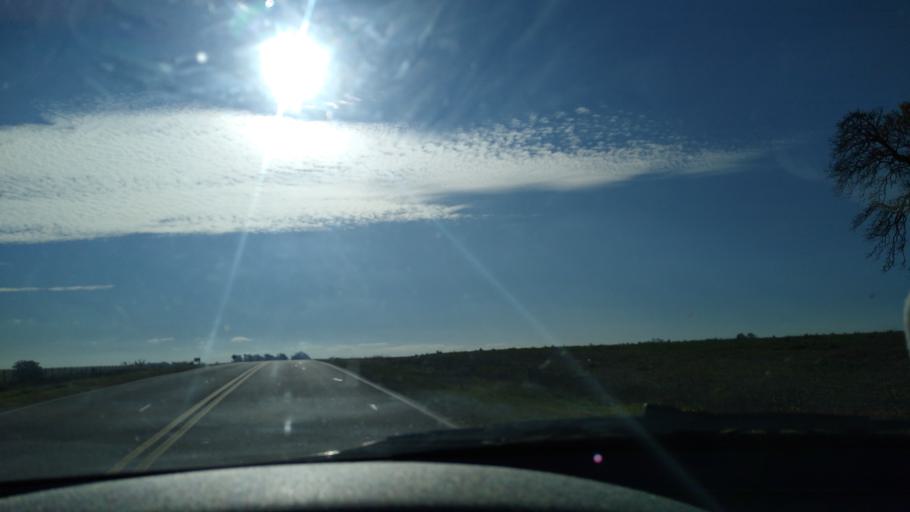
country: AR
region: Entre Rios
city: Aranguren
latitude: -32.3448
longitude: -60.3699
